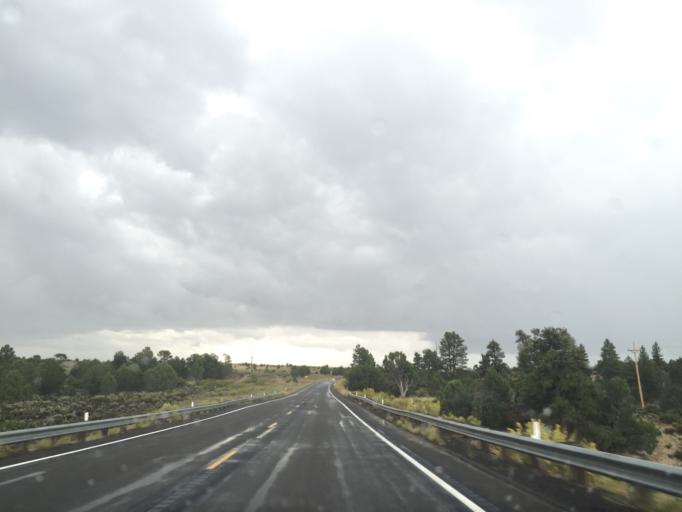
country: US
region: Utah
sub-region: Kane County
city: Kanab
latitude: 37.2328
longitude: -112.7354
